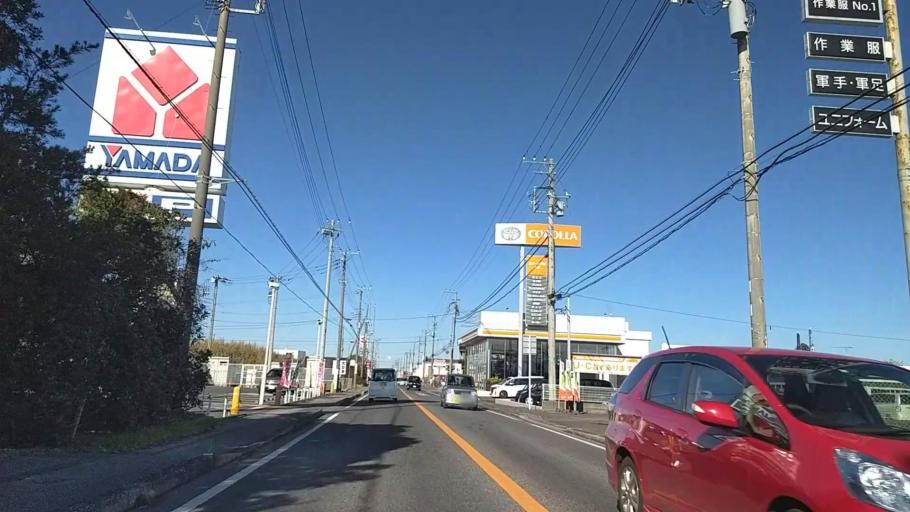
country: JP
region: Chiba
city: Ohara
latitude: 35.2691
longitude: 140.3941
